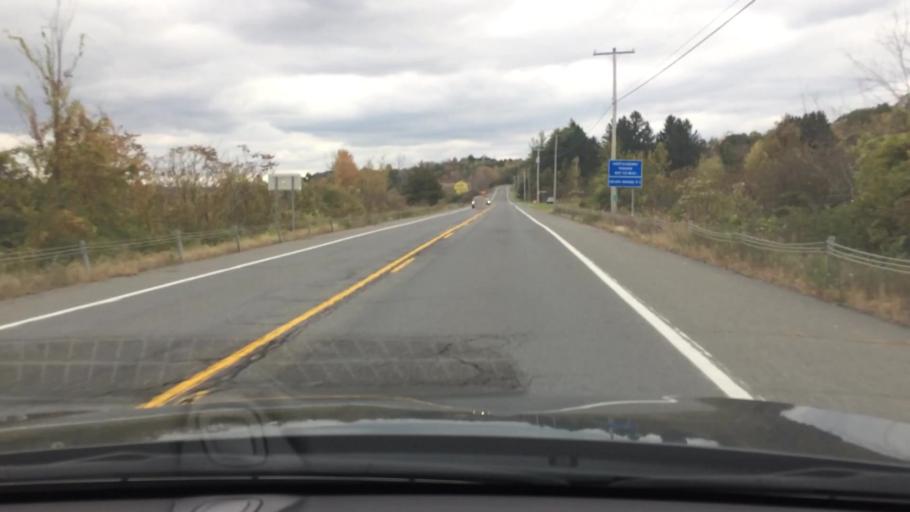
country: US
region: New York
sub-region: Columbia County
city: Oakdale
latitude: 42.1433
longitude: -73.7415
